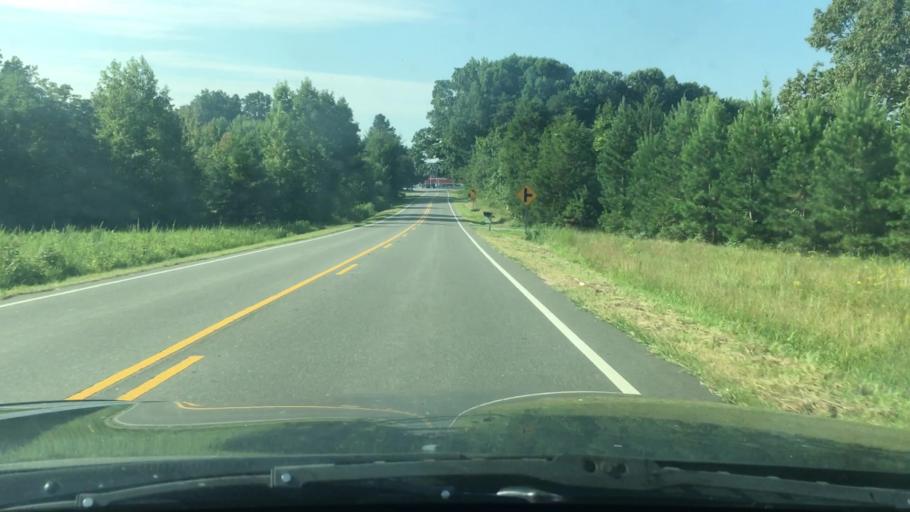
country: US
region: North Carolina
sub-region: Caswell County
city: Yanceyville
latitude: 36.2728
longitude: -79.3479
